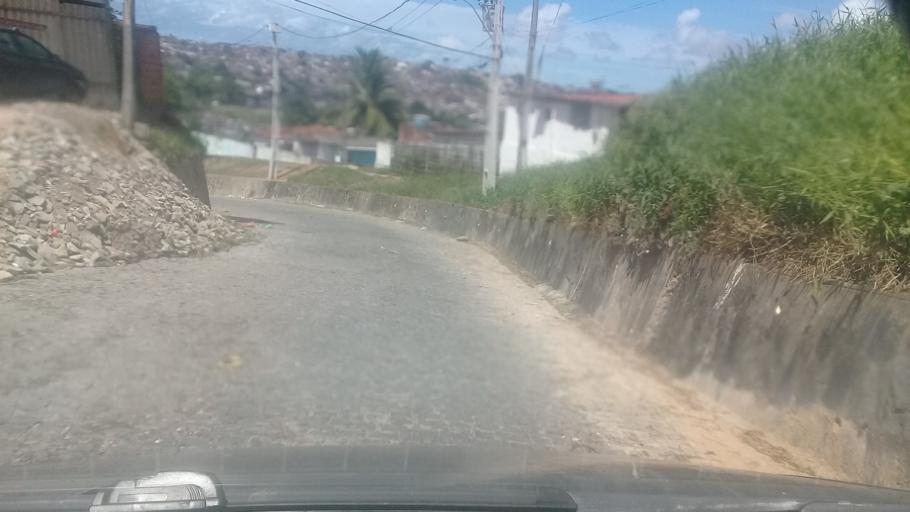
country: BR
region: Pernambuco
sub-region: Jaboatao Dos Guararapes
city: Jaboatao dos Guararapes
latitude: -8.1220
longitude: -34.9453
